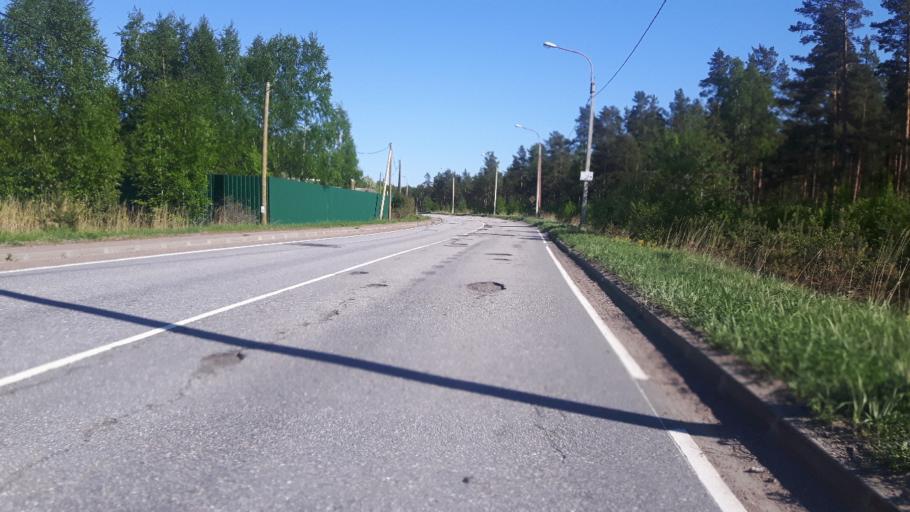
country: RU
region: Leningrad
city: Sosnovyy Bor
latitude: 60.1907
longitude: 29.0147
